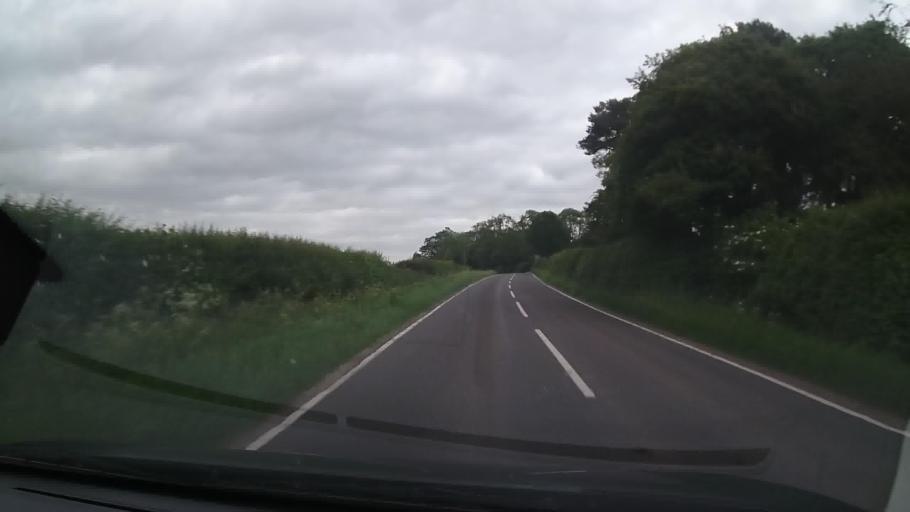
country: GB
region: England
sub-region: Shropshire
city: Clive
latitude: 52.8253
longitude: -2.7382
